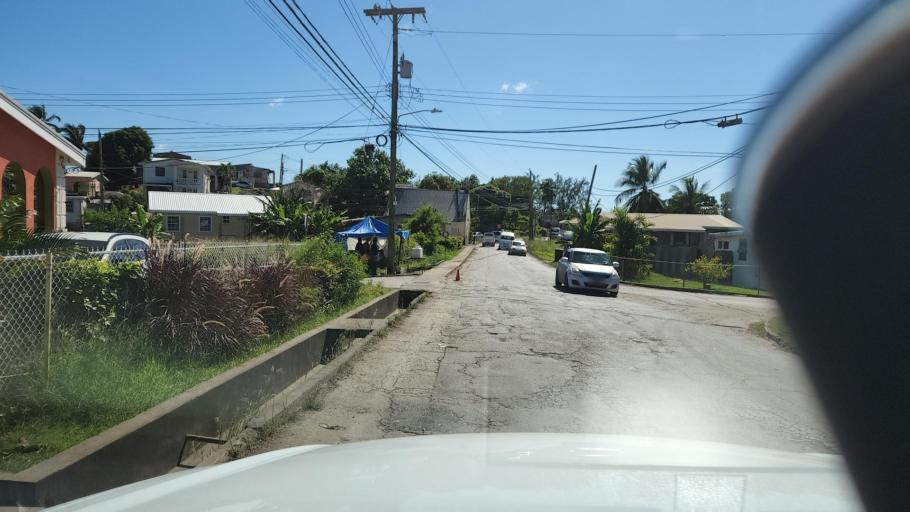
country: BB
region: Saint Thomas
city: Welchman Hall
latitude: 13.1643
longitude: -59.6008
